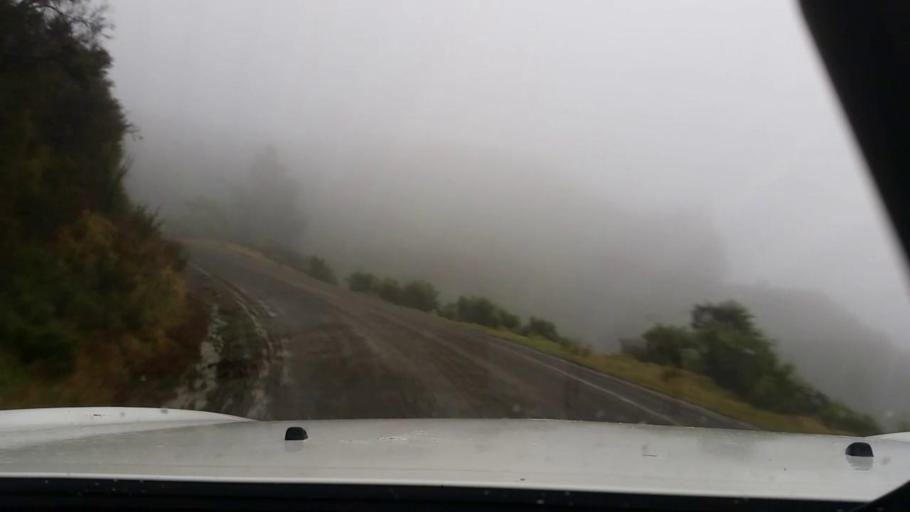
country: NZ
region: Wellington
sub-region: Masterton District
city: Masterton
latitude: -41.2441
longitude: 175.8776
